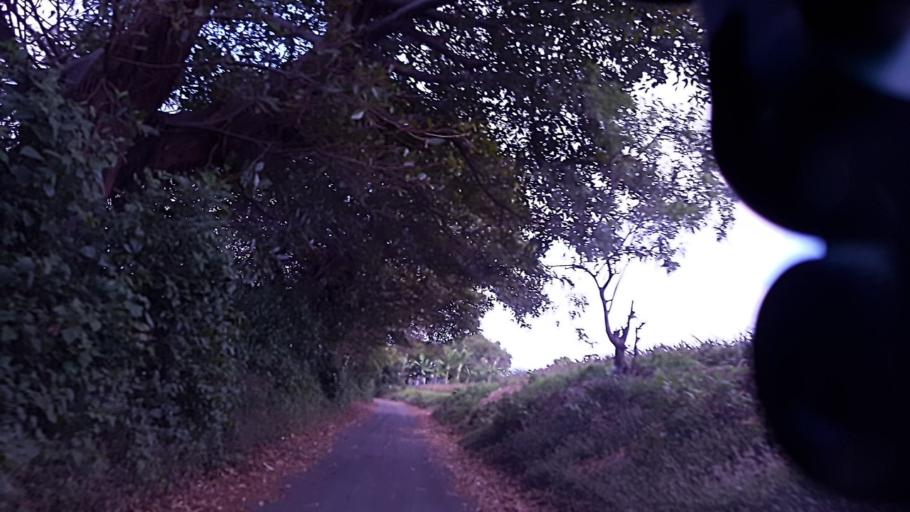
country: NI
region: Masaya
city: Ticuantepe
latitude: 11.9877
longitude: -86.2265
